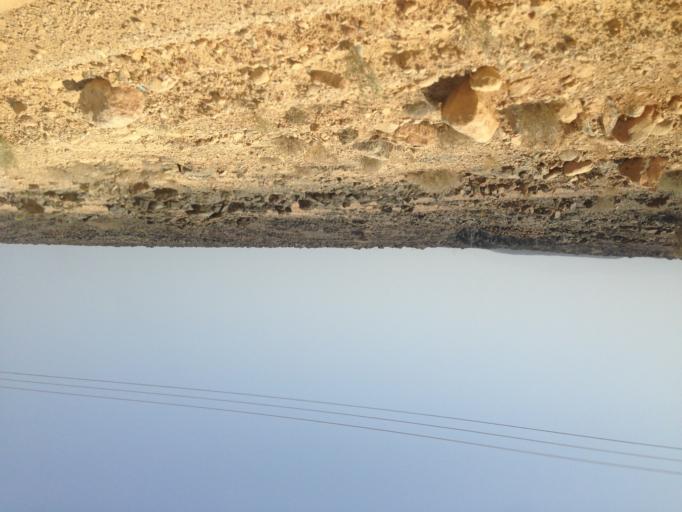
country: OM
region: Ash Sharqiyah
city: Ibra'
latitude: 23.0850
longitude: 58.9401
